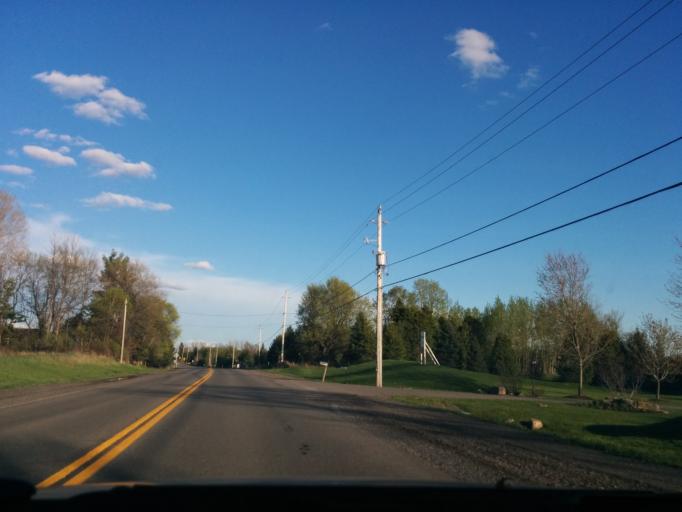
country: CA
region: Ontario
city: Bells Corners
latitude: 45.2140
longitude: -75.6570
